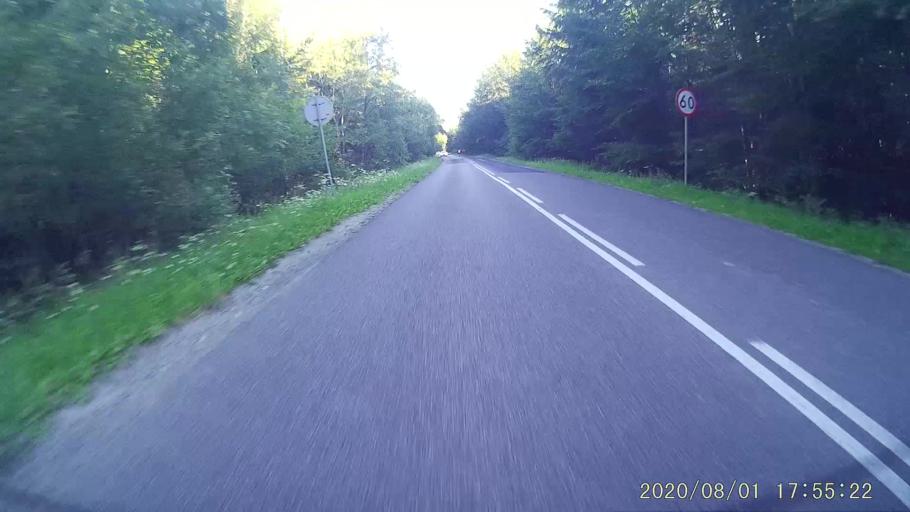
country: PL
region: Lesser Poland Voivodeship
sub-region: Powiat tatrzanski
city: Bukowina Tatrzanska
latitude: 49.2929
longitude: 20.1009
